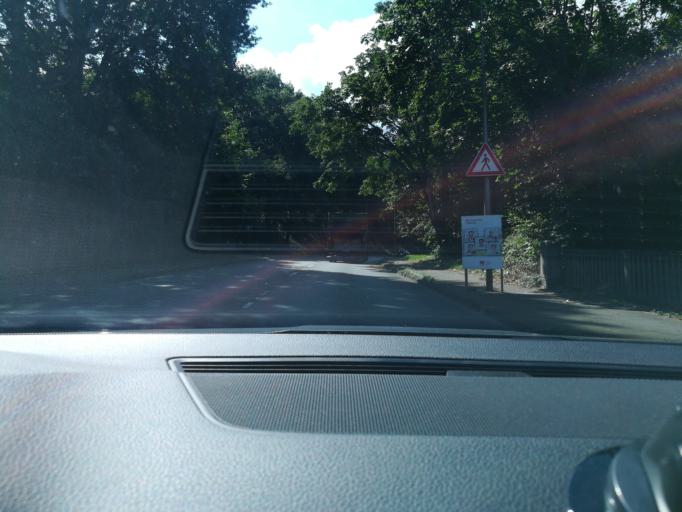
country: DE
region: North Rhine-Westphalia
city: Lubbecke
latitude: 52.3014
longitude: 8.6207
